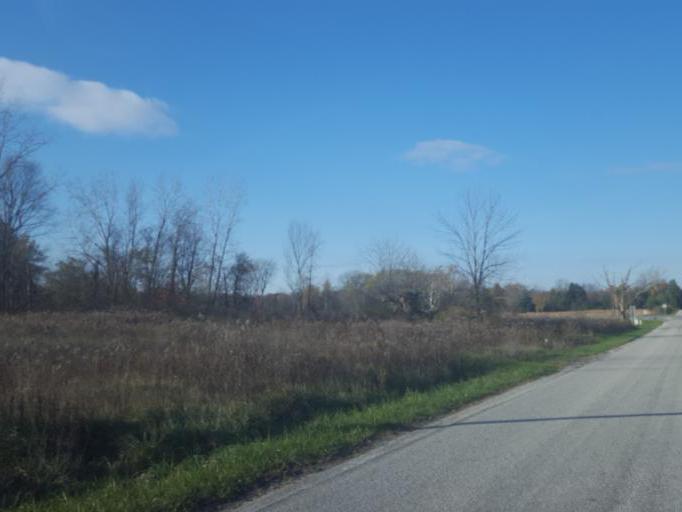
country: US
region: Ohio
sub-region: Crawford County
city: Galion
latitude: 40.6392
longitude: -82.7635
